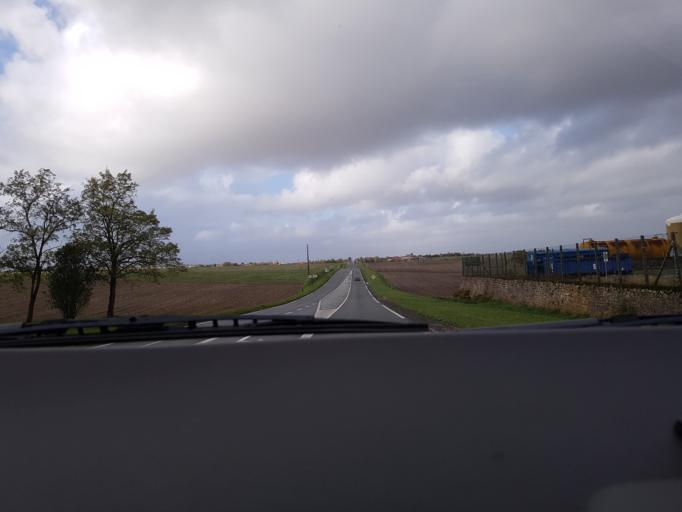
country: FR
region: Poitou-Charentes
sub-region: Departement de la Charente-Maritime
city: Pons
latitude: 45.6409
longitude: -0.5800
